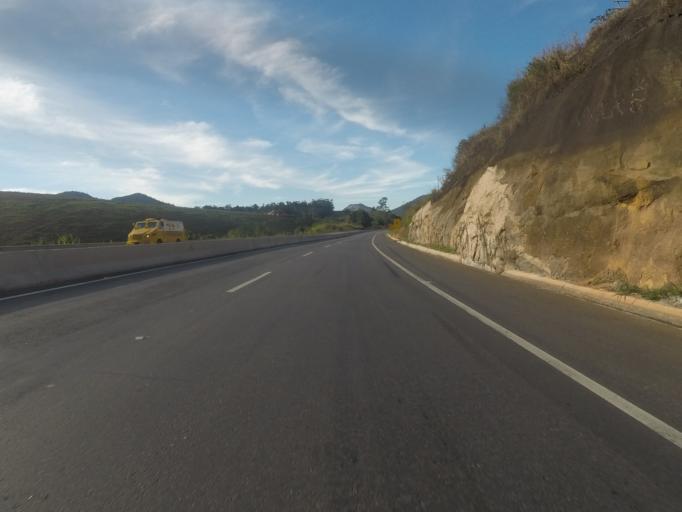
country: BR
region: Espirito Santo
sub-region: Ibiracu
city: Ibiracu
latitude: -19.8418
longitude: -40.3855
